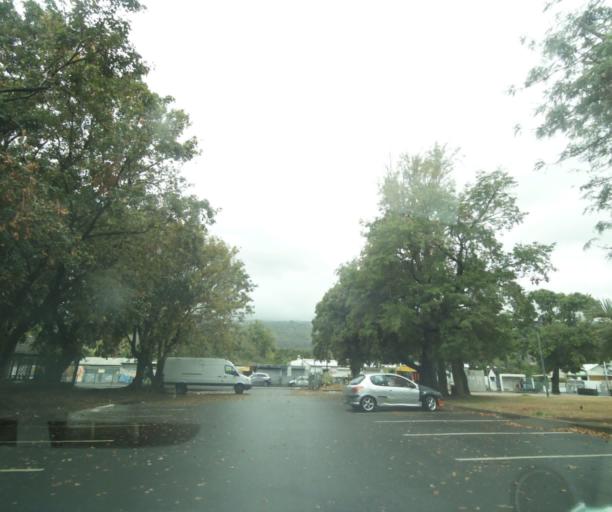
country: RE
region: Reunion
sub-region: Reunion
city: Saint-Paul
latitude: -21.0007
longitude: 55.2808
